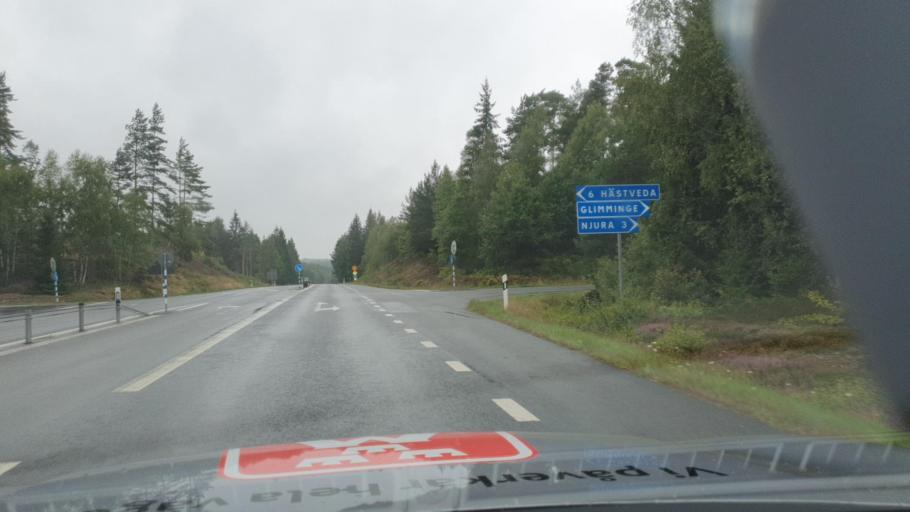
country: SE
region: Skane
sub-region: Ostra Goinge Kommun
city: Broby
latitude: 56.2799
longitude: 14.0207
